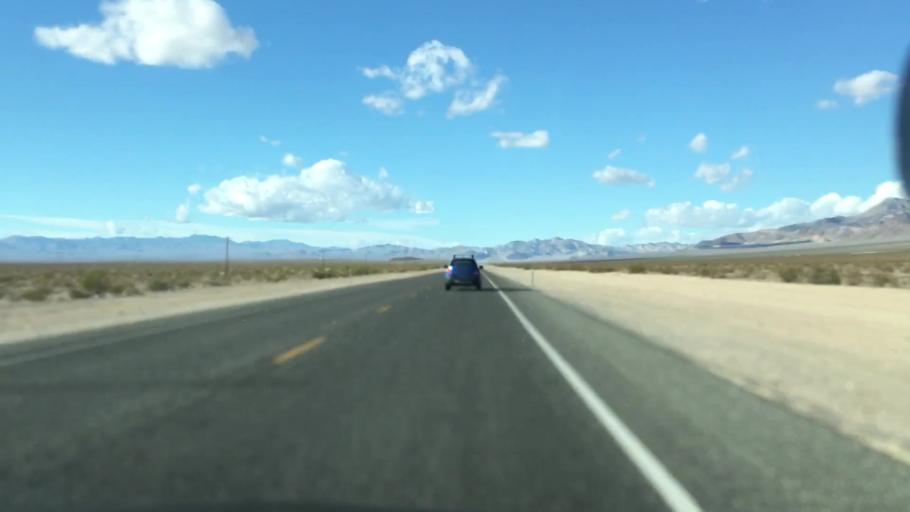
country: US
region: Nevada
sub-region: Nye County
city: Beatty
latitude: 36.7451
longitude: -116.6498
